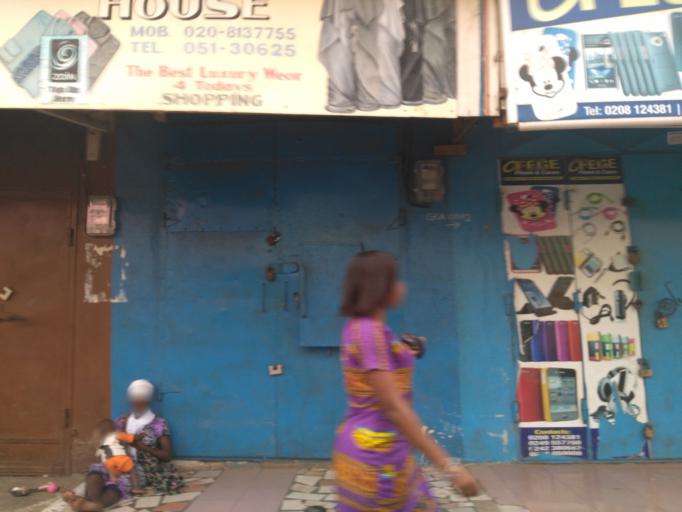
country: GH
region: Ashanti
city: Kumasi
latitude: 6.6920
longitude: -1.6214
